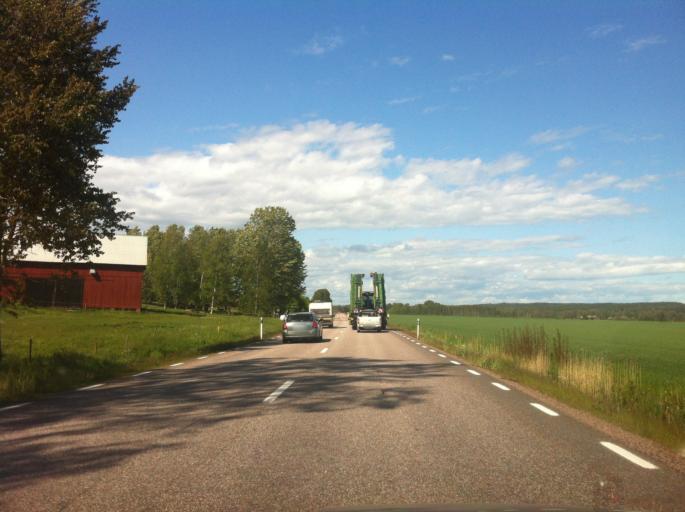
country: SE
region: Vaestra Goetaland
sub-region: Gullspangs Kommun
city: Gullspang
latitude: 59.1053
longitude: 14.1717
